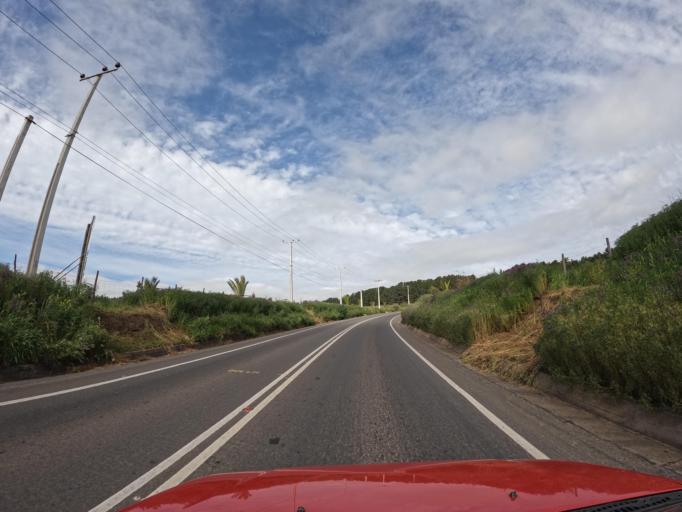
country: CL
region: O'Higgins
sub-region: Provincia de Colchagua
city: Santa Cruz
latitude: -34.3669
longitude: -71.9622
